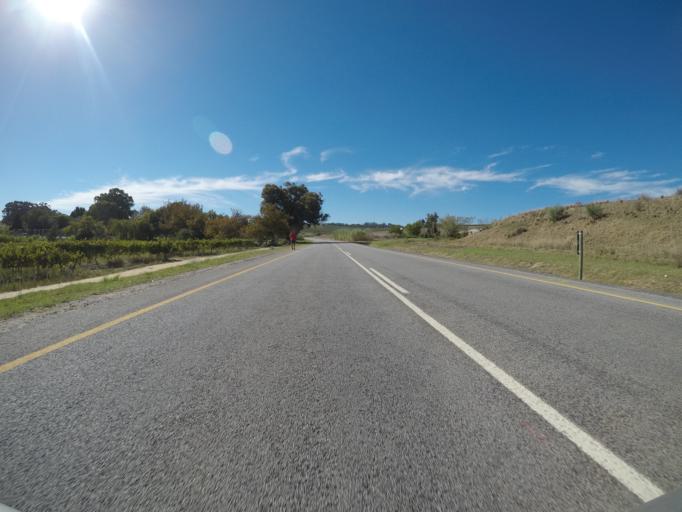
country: ZA
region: Western Cape
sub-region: Cape Winelands District Municipality
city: Stellenbosch
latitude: -33.9793
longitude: 18.7536
